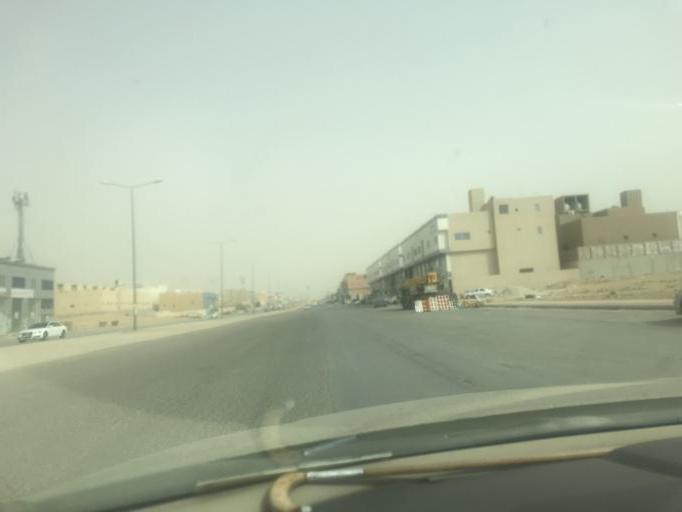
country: SA
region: Ar Riyad
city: Riyadh
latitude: 24.8041
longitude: 46.6039
